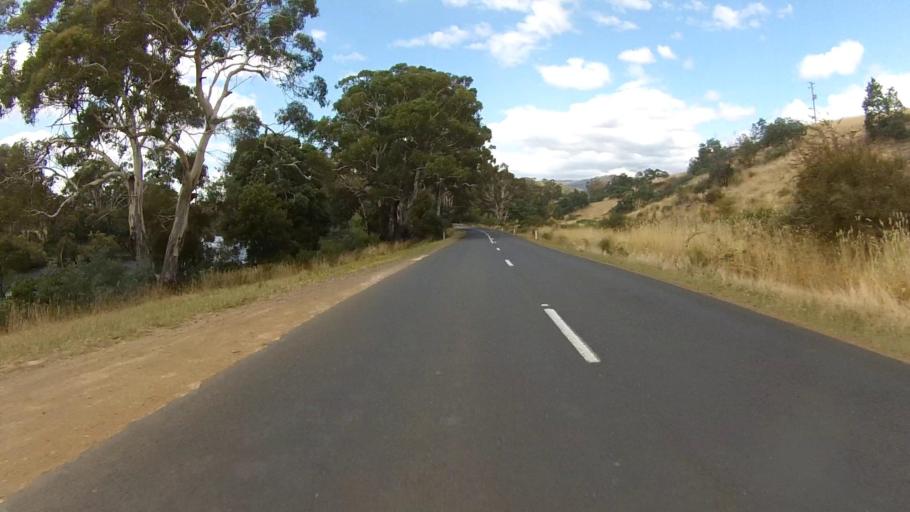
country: AU
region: Tasmania
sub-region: Derwent Valley
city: New Norfolk
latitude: -42.7561
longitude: 146.9856
